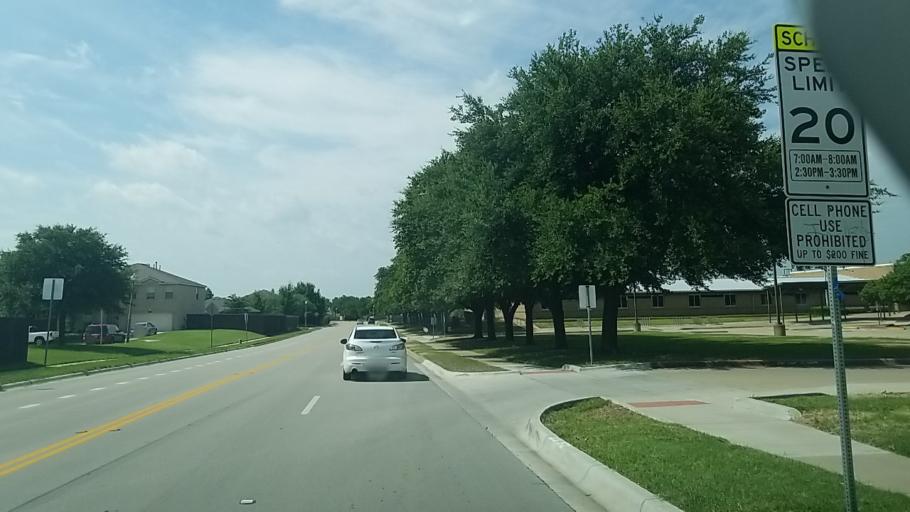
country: US
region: Texas
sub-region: Denton County
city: Corinth
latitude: 33.1470
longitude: -97.1200
